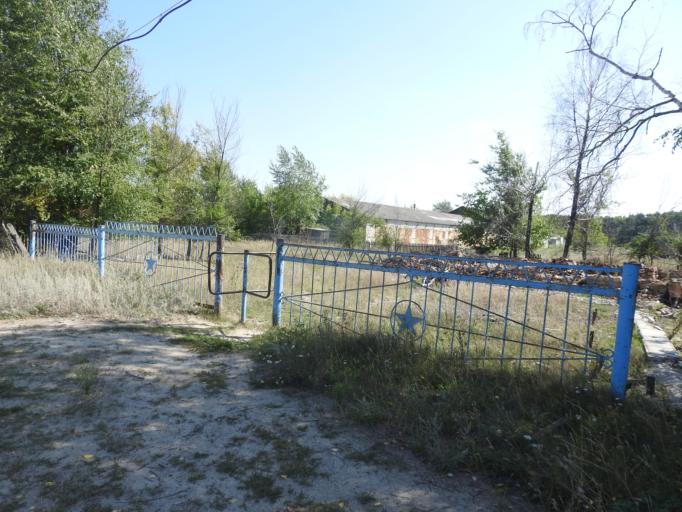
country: RU
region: Saratov
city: Lysyye Gory
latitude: 51.3114
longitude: 45.0109
